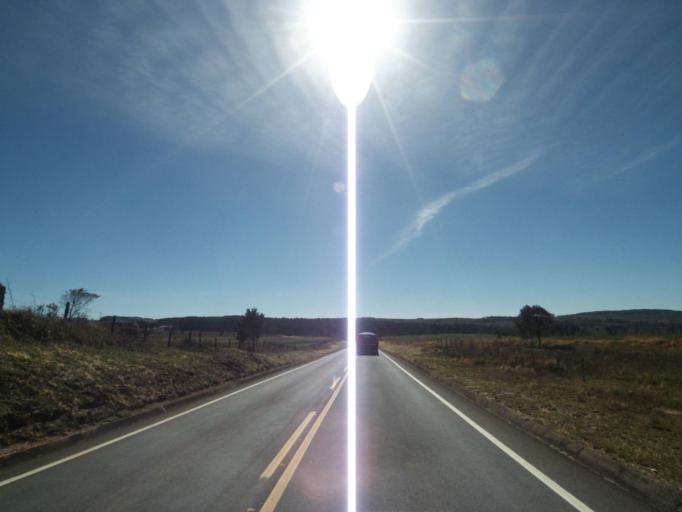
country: BR
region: Parana
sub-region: Castro
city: Castro
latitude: -24.7351
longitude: -50.1818
